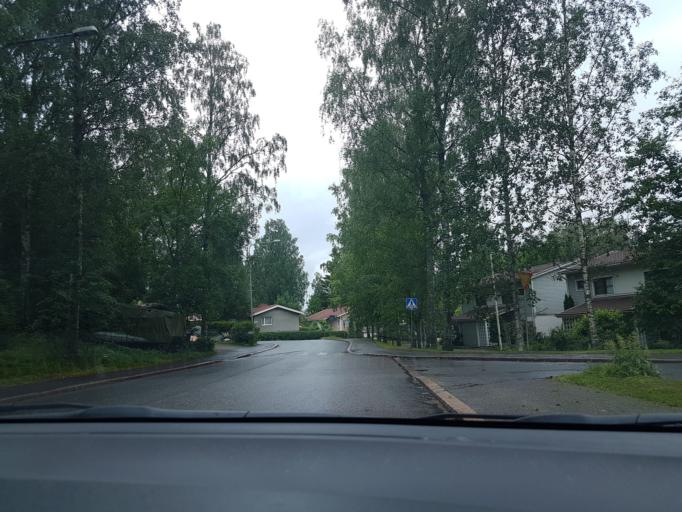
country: FI
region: Uusimaa
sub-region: Helsinki
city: Vantaa
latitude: 60.2279
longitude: 25.1060
